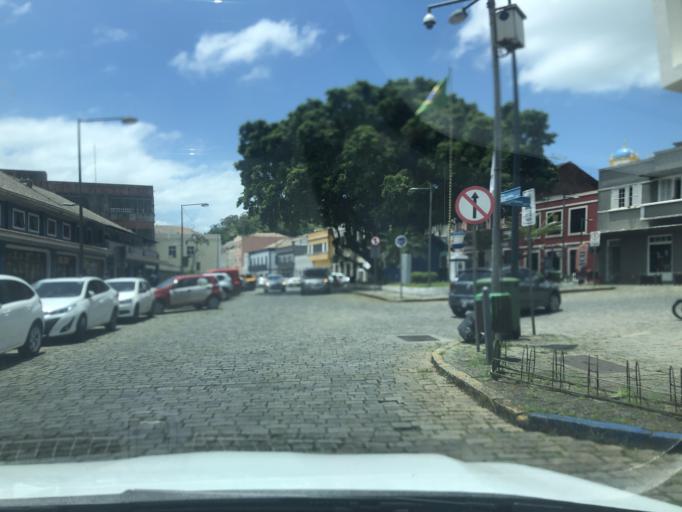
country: BR
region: Santa Catarina
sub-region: Sao Francisco Do Sul
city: Sao Francisco do Sul
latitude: -26.2446
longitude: -48.6398
